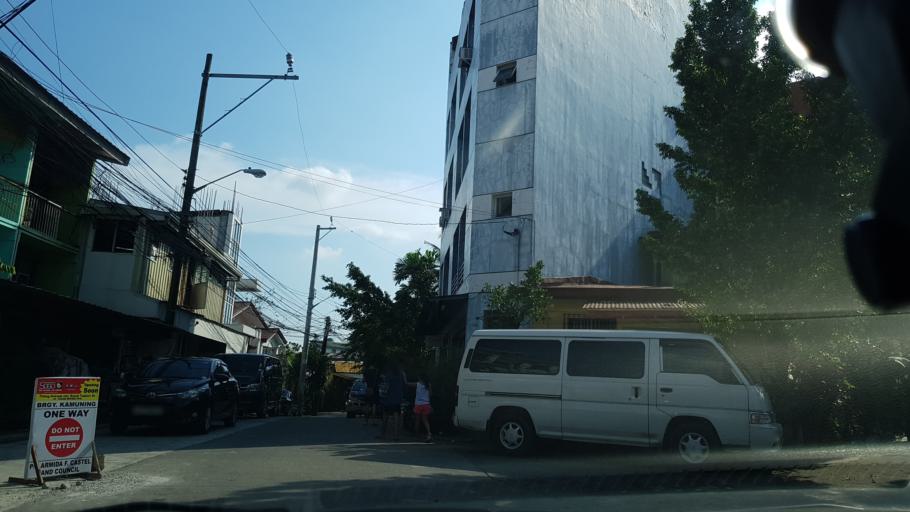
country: PH
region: Metro Manila
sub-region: Quezon City
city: Quezon City
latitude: 14.6289
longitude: 121.0439
